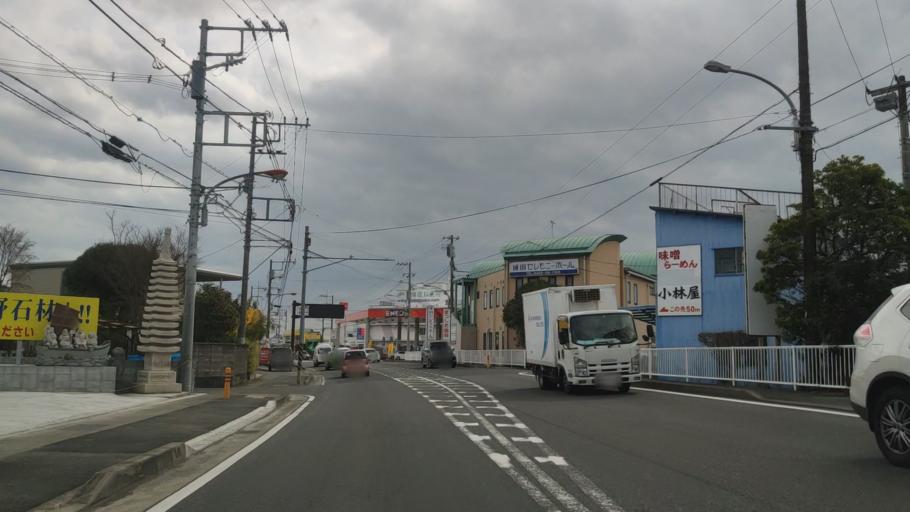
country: JP
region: Kanagawa
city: Odawara
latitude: 35.2893
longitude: 139.1679
